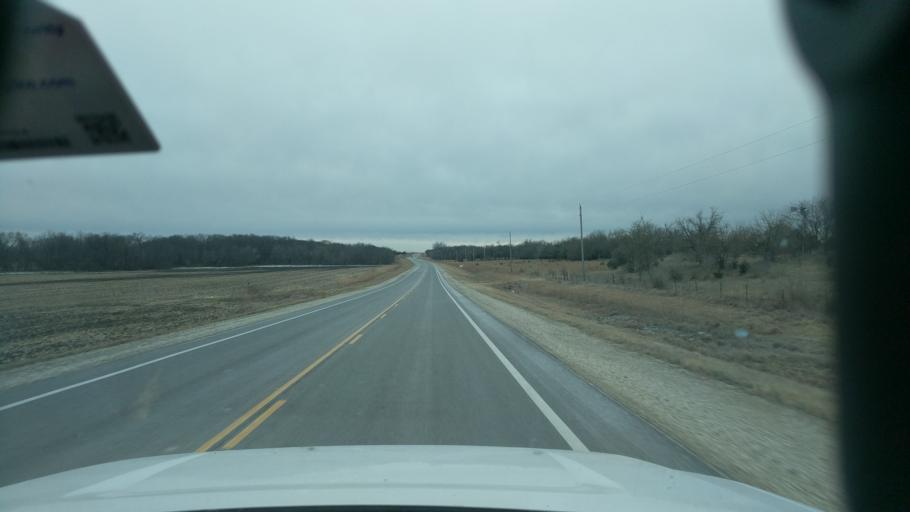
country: US
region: Kansas
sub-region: Marion County
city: Marion
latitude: 38.4762
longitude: -96.9578
